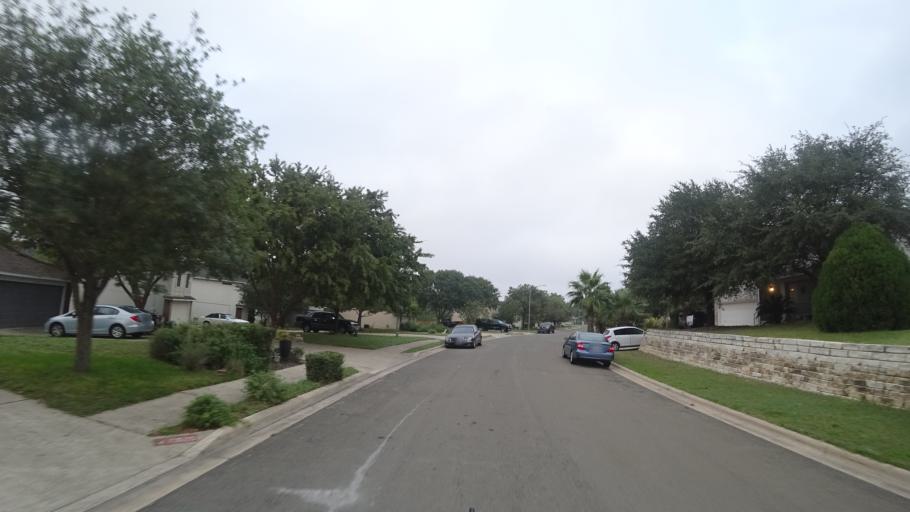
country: US
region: Texas
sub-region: Travis County
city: Wells Branch
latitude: 30.3664
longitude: -97.6710
